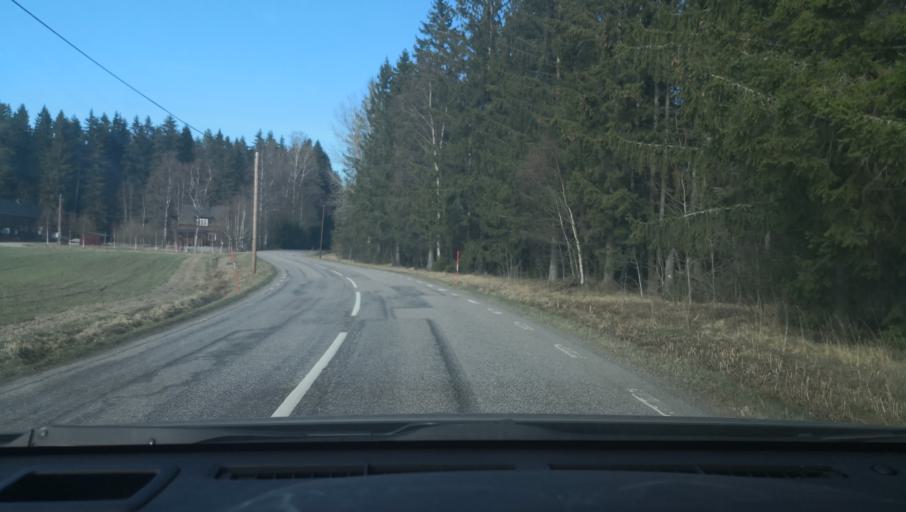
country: SE
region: Uppsala
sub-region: Heby Kommun
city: Heby
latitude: 59.9714
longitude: 16.8971
